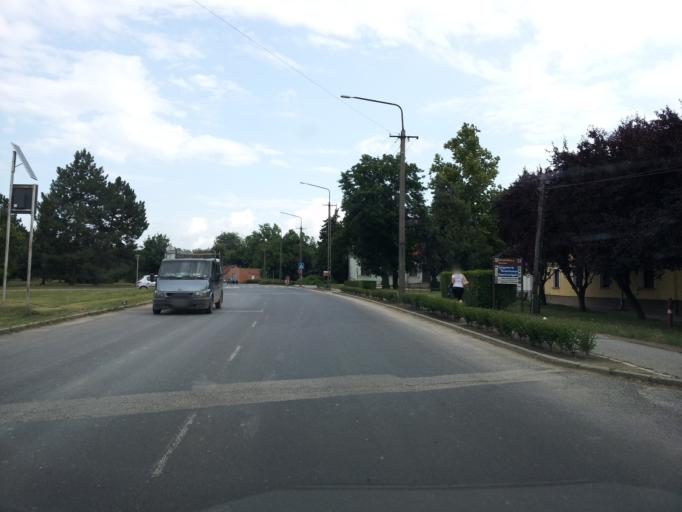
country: HU
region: Fejer
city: Enying
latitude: 46.9277
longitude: 18.2444
